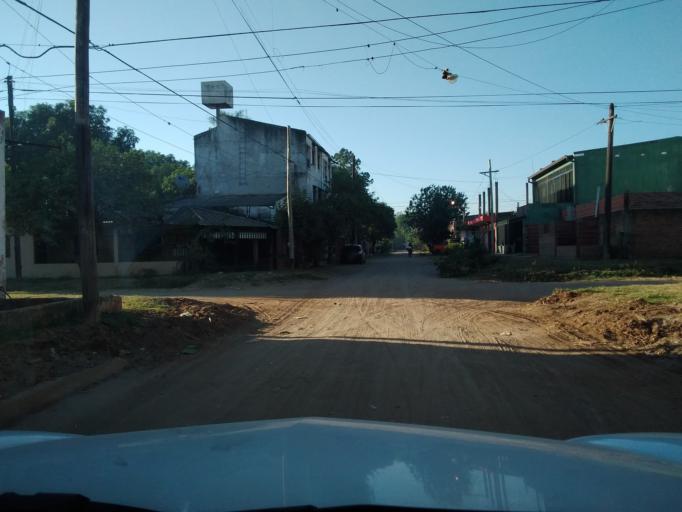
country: AR
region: Corrientes
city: Corrientes
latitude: -27.4782
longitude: -58.7862
